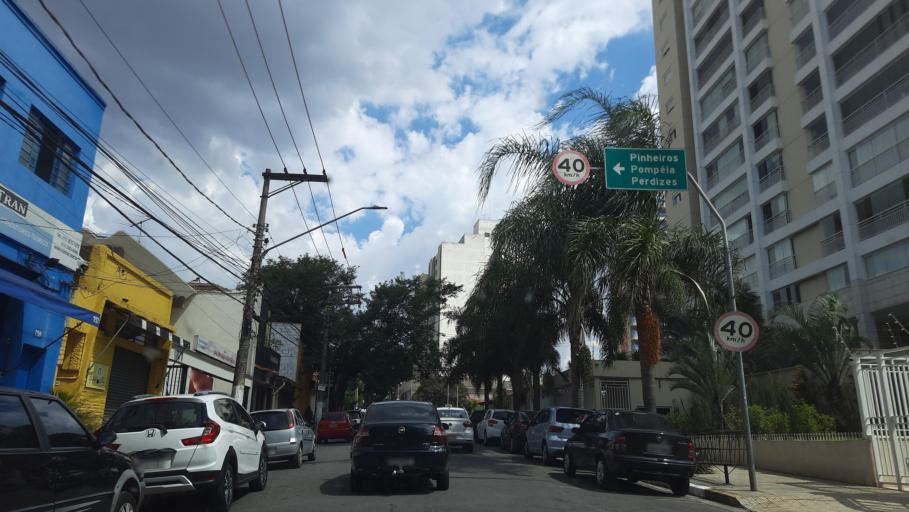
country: BR
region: Sao Paulo
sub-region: Sao Paulo
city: Sao Paulo
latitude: -23.5275
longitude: -46.7007
